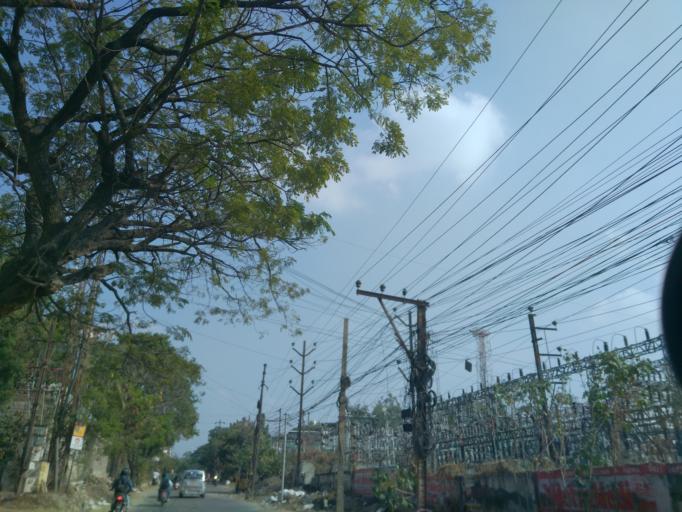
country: IN
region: Telangana
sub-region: Rangareddi
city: Kukatpalli
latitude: 17.4303
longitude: 78.4039
